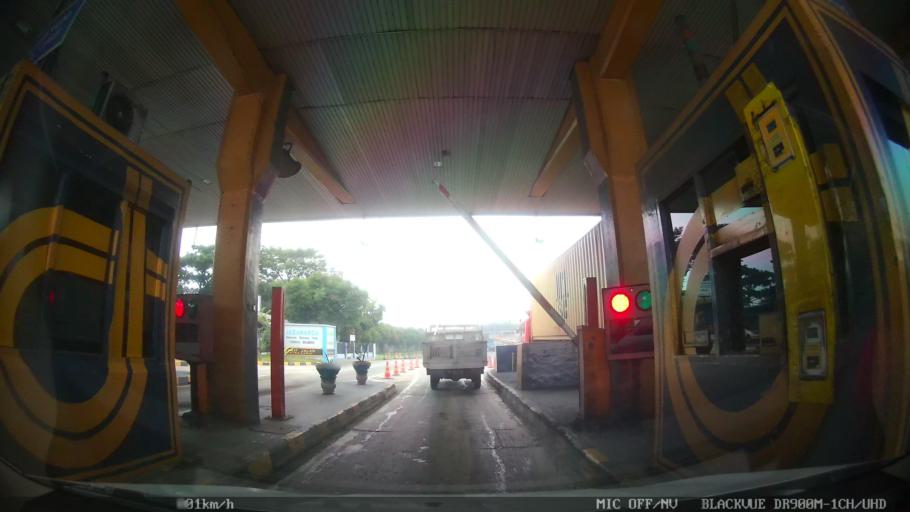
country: ID
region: North Sumatra
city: Deli Tua
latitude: 3.5375
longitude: 98.7219
